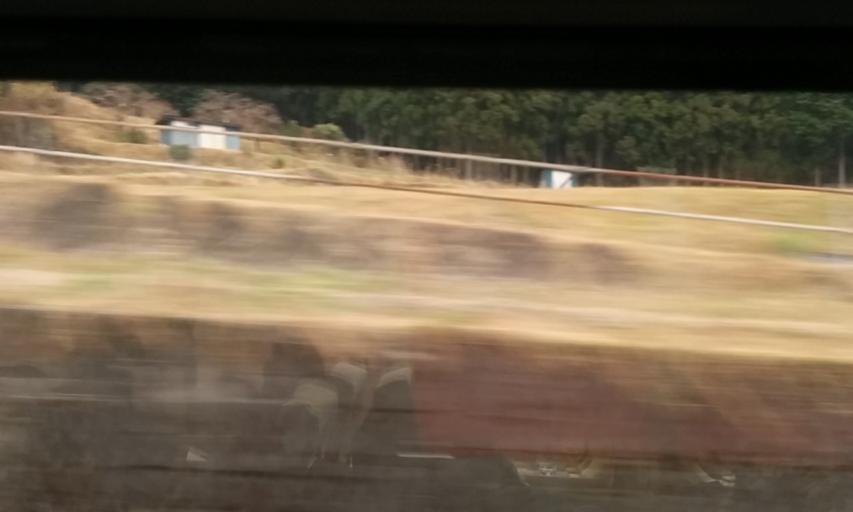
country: JP
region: Nagano
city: Ina
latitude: 35.7566
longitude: 137.7100
